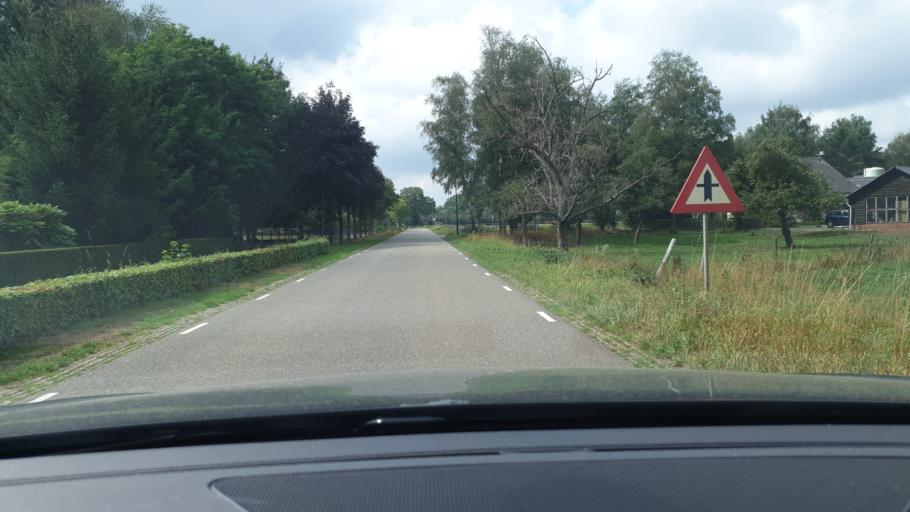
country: NL
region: North Brabant
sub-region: Gemeente Veldhoven
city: Oerle
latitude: 51.4513
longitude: 5.3507
